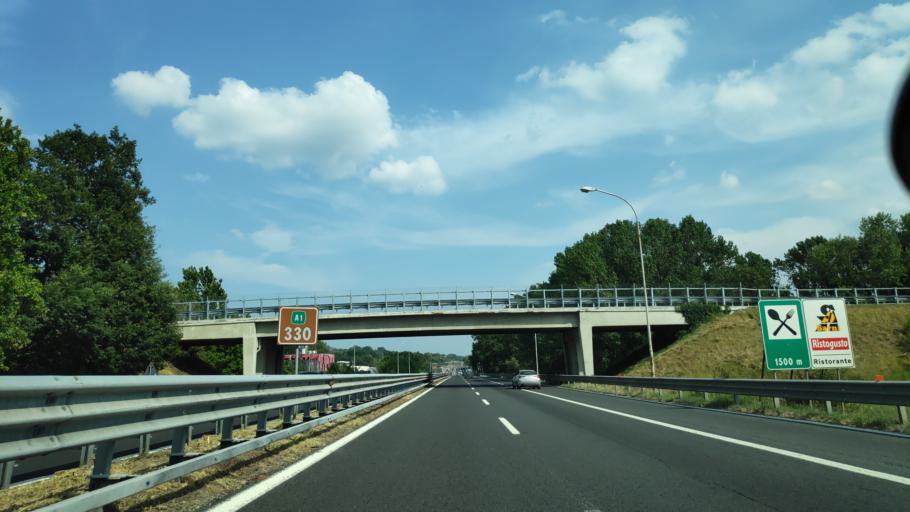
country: IT
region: Umbria
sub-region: Provincia di Terni
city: Attigliano
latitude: 42.5086
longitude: 12.2948
